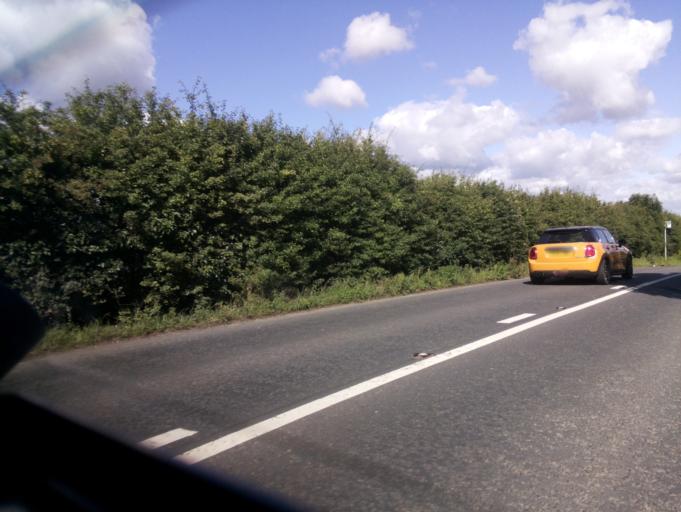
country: GB
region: England
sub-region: Gloucestershire
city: Newent
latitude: 51.9114
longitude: -2.3438
